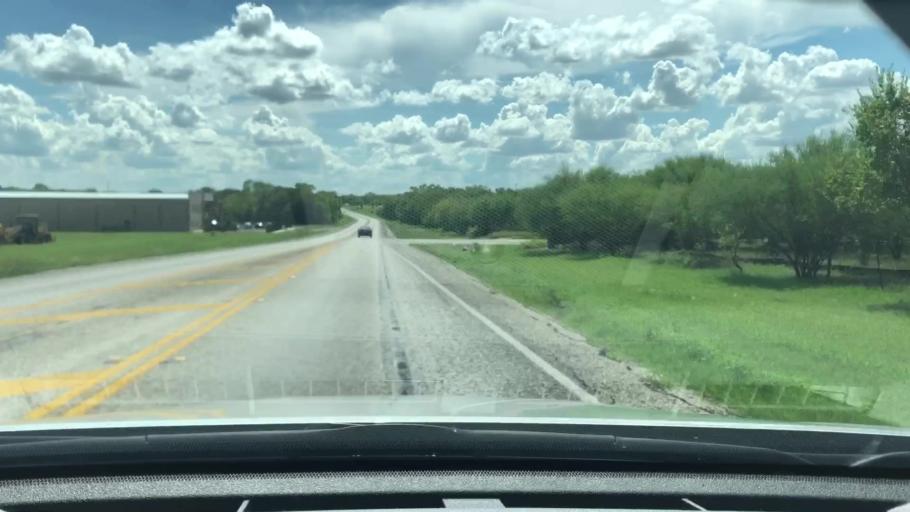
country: US
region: Texas
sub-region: Bexar County
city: Converse
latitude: 29.5263
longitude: -98.3098
